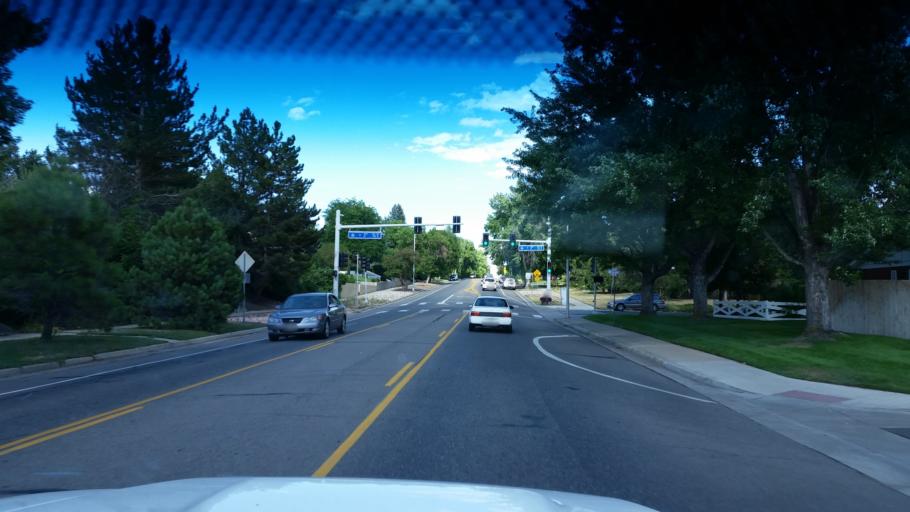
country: US
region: Colorado
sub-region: Broomfield County
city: Broomfield
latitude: 39.9238
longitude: -105.0788
